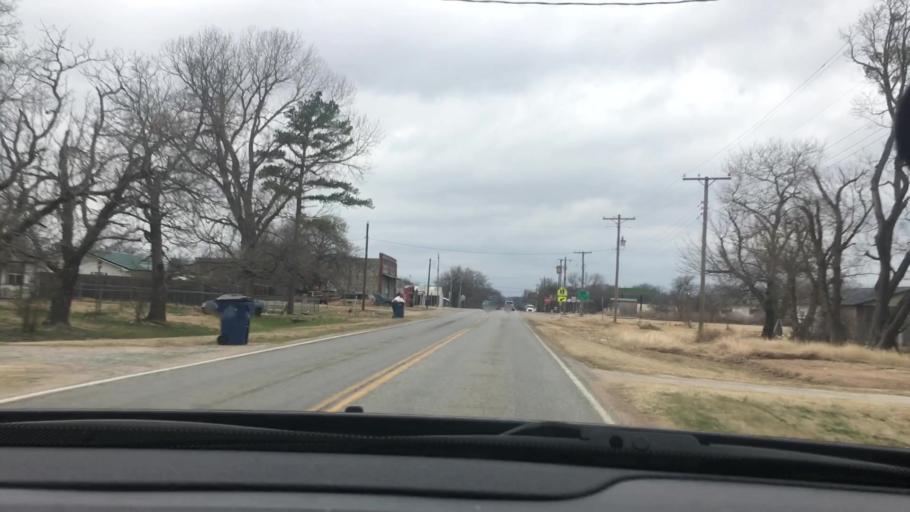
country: US
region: Oklahoma
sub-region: Coal County
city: Coalgate
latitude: 34.3750
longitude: -96.4222
